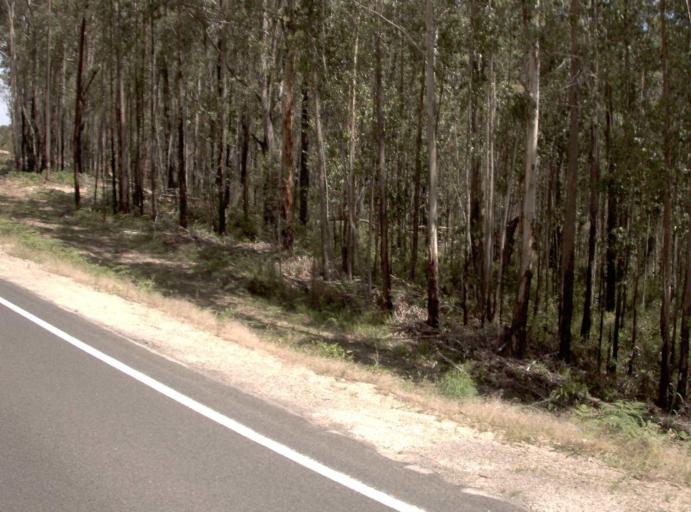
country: AU
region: New South Wales
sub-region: Bombala
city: Bombala
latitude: -37.5633
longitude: 149.2506
